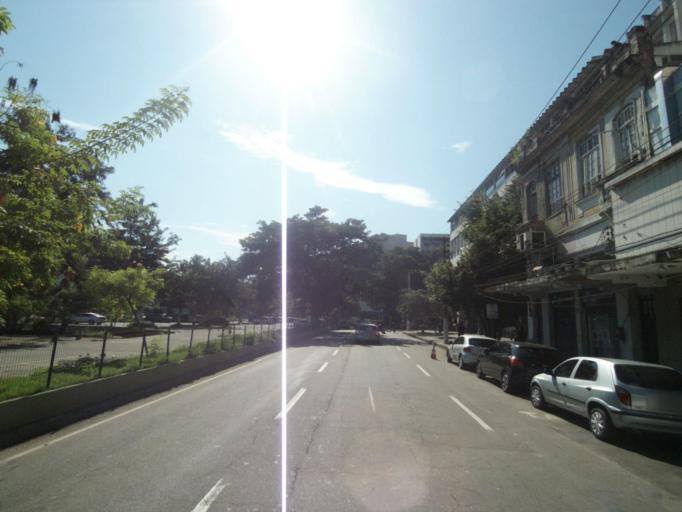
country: BR
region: Rio de Janeiro
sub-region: Niteroi
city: Niteroi
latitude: -22.8965
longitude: -43.1263
